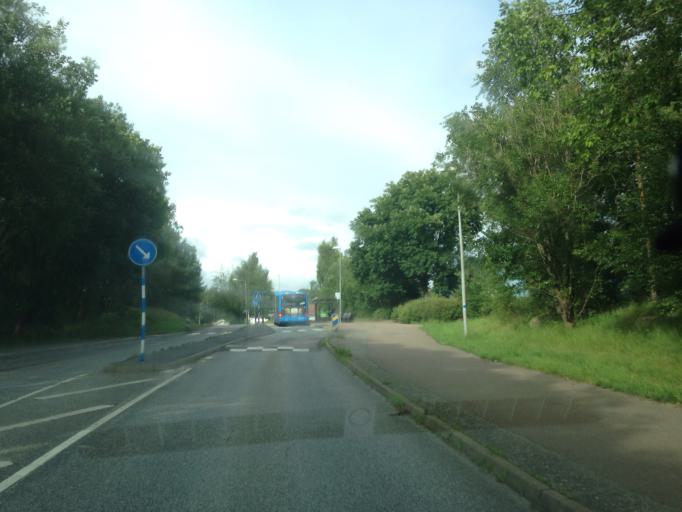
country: SE
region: Vaestra Goetaland
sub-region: Goteborg
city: Goeteborg
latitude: 57.7611
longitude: 11.9675
